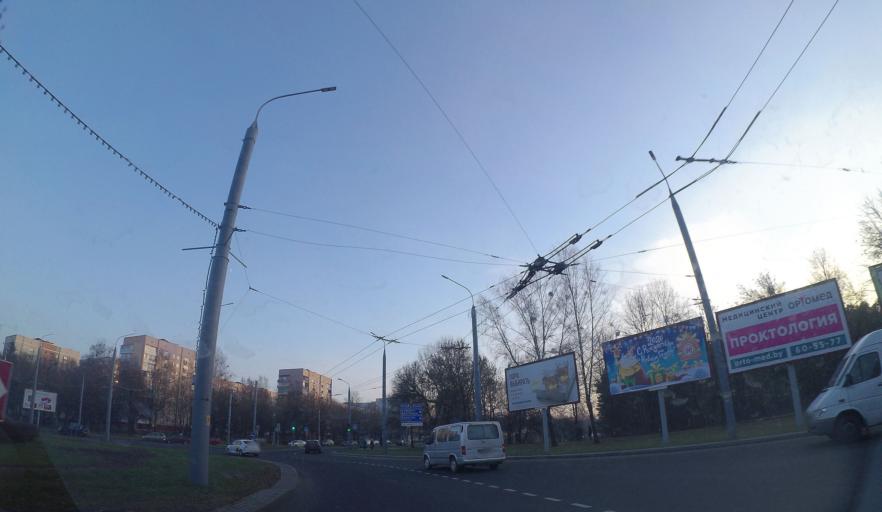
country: BY
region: Grodnenskaya
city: Hrodna
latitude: 53.6967
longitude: 23.7999
